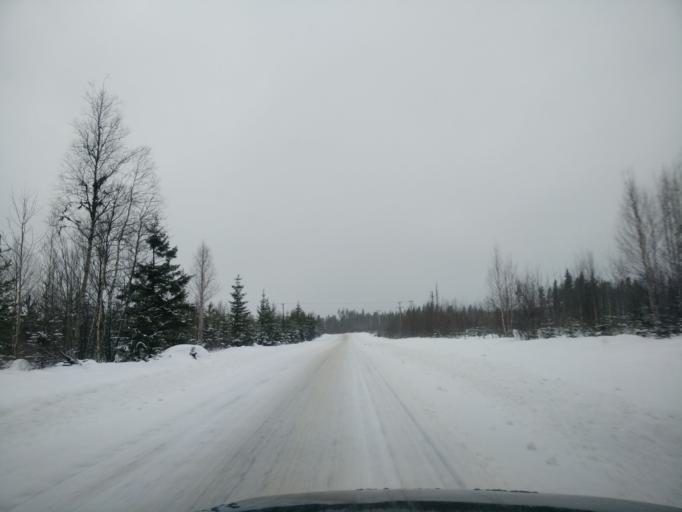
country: SE
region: Vaesternorrland
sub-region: Ange Kommun
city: Ange
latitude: 62.4702
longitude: 15.4634
